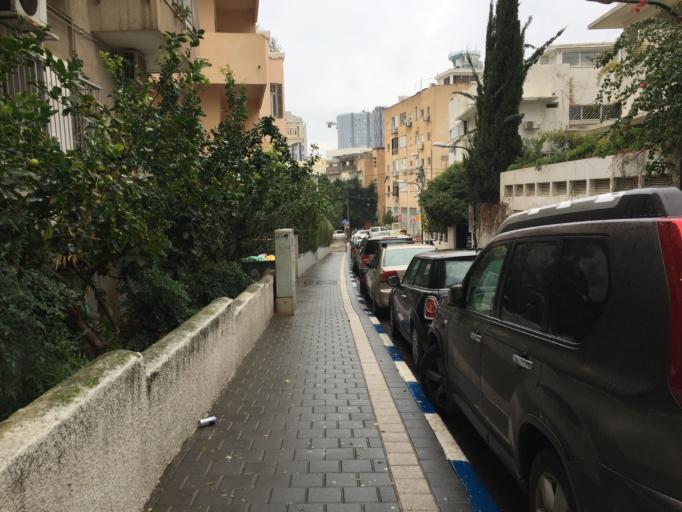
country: IL
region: Tel Aviv
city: Tel Aviv
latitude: 32.0735
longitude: 34.7699
